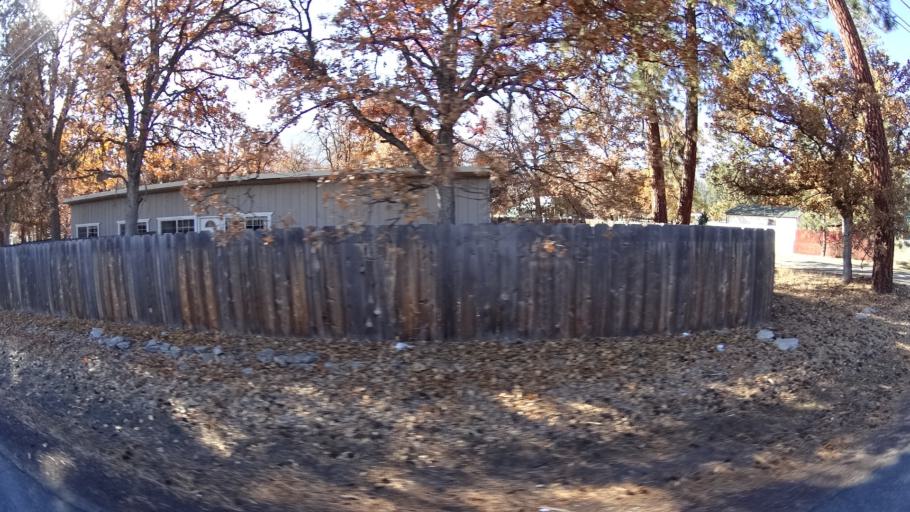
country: US
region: California
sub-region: Siskiyou County
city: Yreka
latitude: 41.6653
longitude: -122.6070
